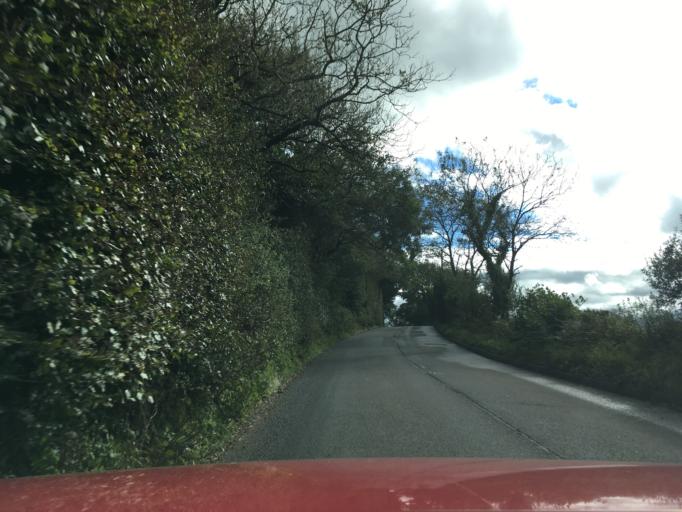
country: GB
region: England
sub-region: Devon
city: Kingsbridge
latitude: 50.3530
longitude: -3.7270
